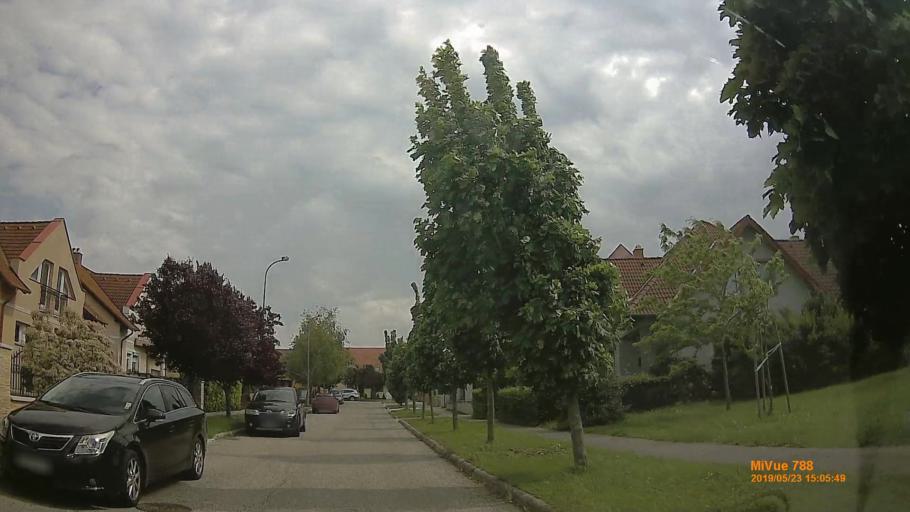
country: HU
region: Veszprem
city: Veszprem
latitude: 47.1153
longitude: 17.9208
